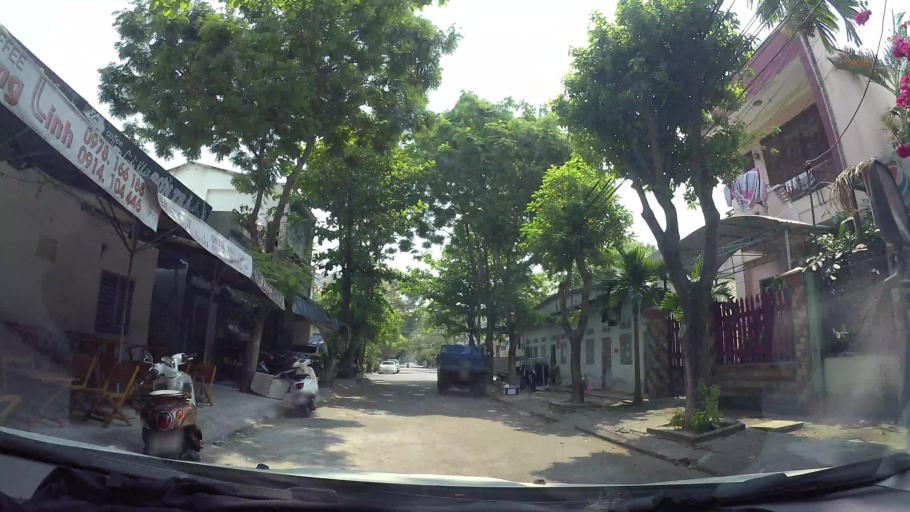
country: VN
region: Da Nang
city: Cam Le
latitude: 16.0173
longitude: 108.2070
